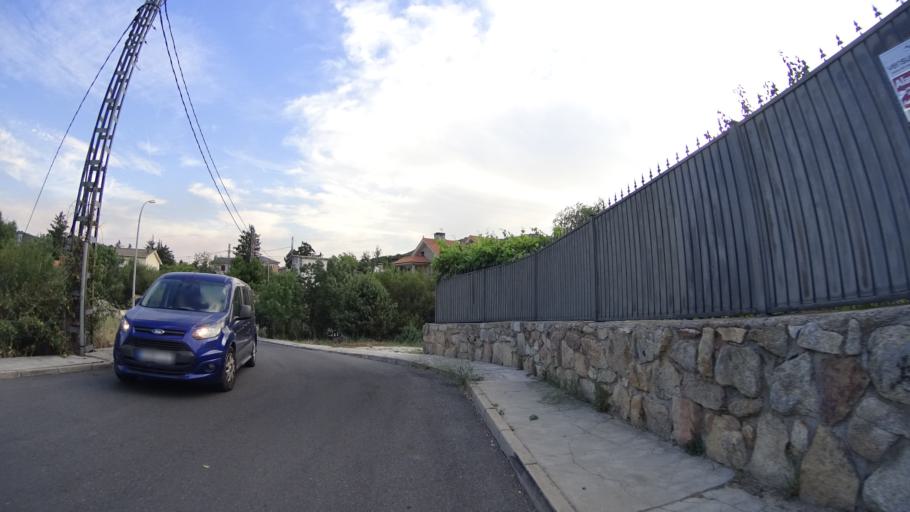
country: ES
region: Madrid
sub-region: Provincia de Madrid
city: Becerril de la Sierra
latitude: 40.7115
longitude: -3.9989
